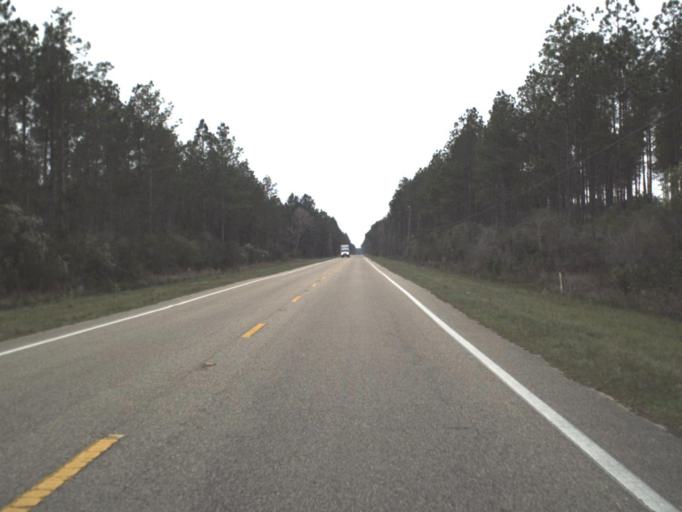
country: US
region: Florida
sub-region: Gulf County
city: Port Saint Joe
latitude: 29.8656
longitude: -85.2389
